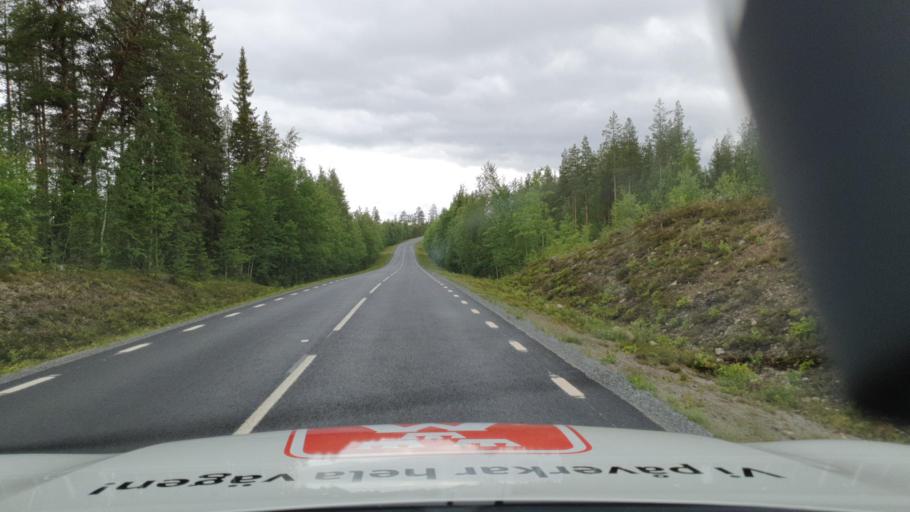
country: SE
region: Vaesterbotten
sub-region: Dorotea Kommun
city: Dorotea
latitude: 64.2018
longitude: 16.5684
